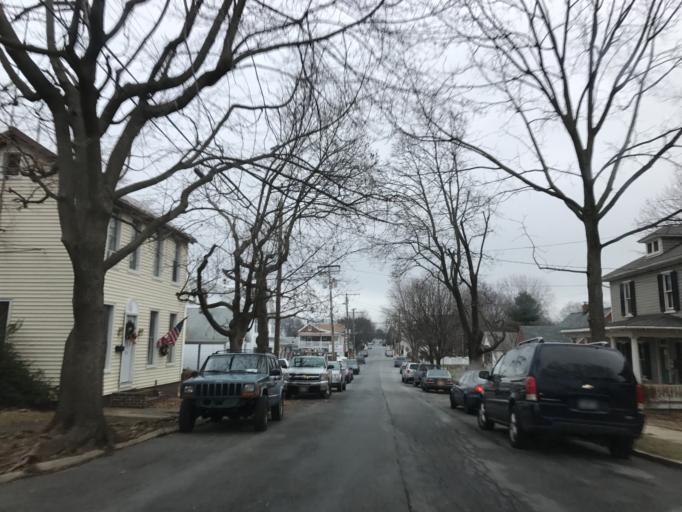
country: US
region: Maryland
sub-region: Carroll County
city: Westminster
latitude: 39.5666
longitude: -76.9912
